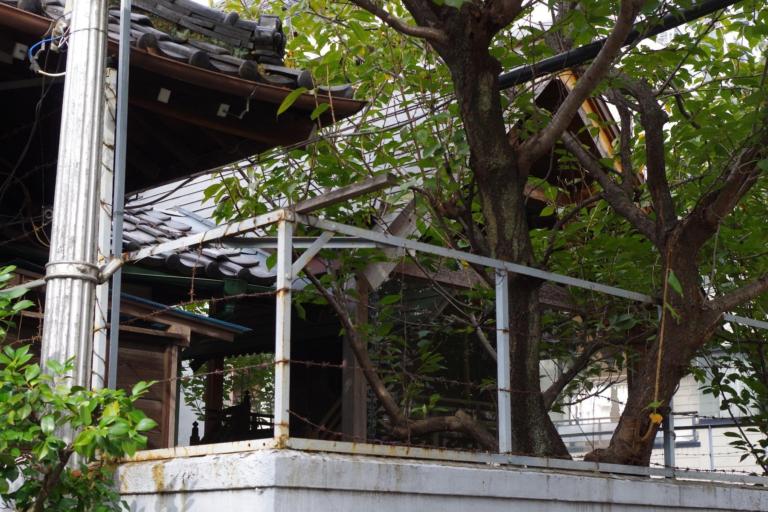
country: JP
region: Tokyo
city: Urayasu
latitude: 35.7083
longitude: 139.8123
